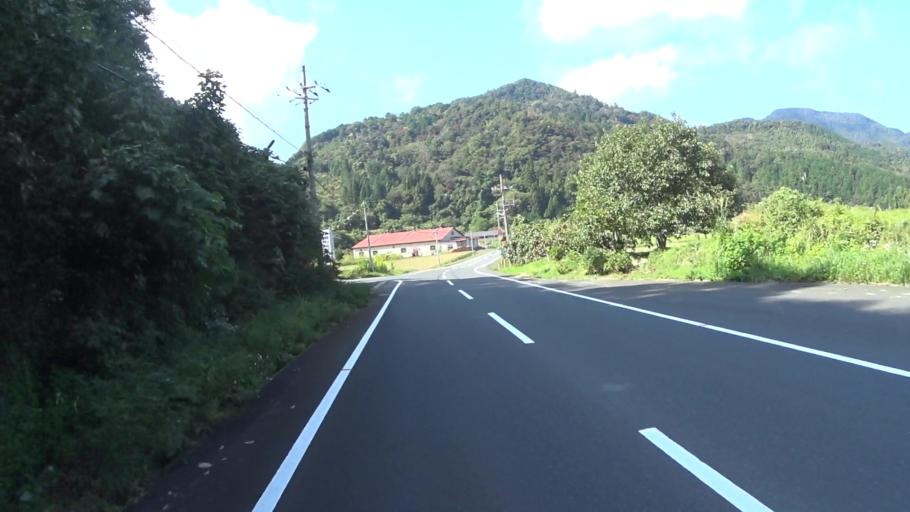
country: JP
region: Kyoto
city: Miyazu
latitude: 35.7092
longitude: 135.2526
